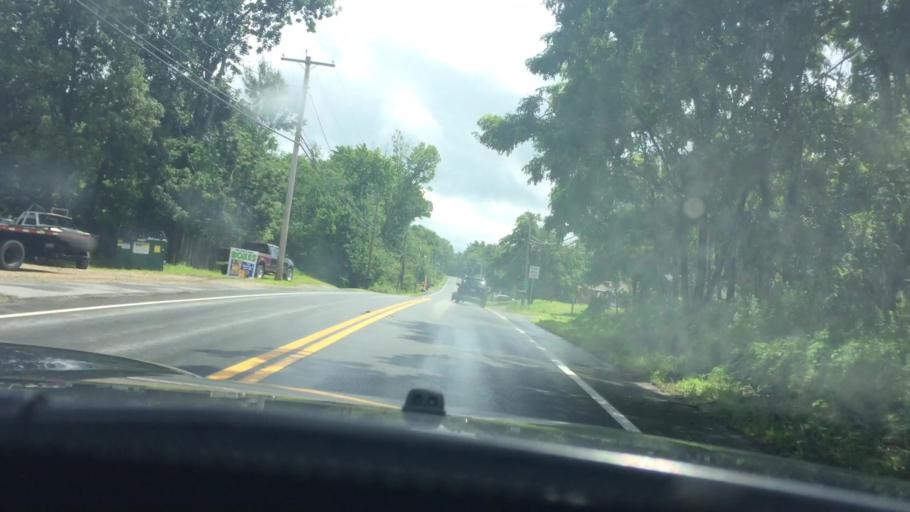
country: US
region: Massachusetts
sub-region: Worcester County
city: Phillipston
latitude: 42.5733
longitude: -72.1619
